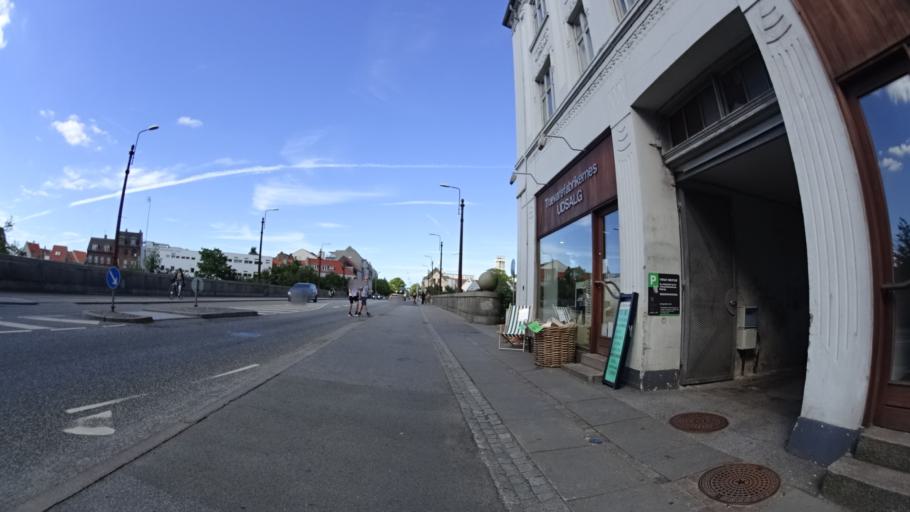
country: DK
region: Central Jutland
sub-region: Arhus Kommune
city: Arhus
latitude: 56.1483
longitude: 10.1968
